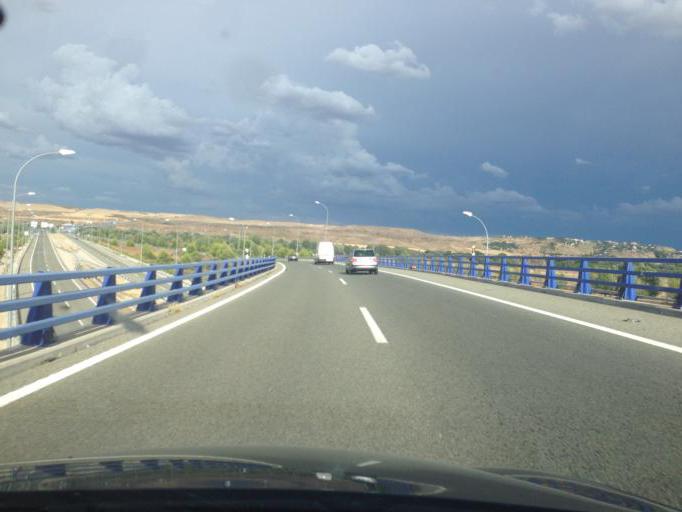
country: ES
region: Madrid
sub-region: Provincia de Madrid
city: San Sebastian de los Reyes
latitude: 40.5428
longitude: -3.5679
